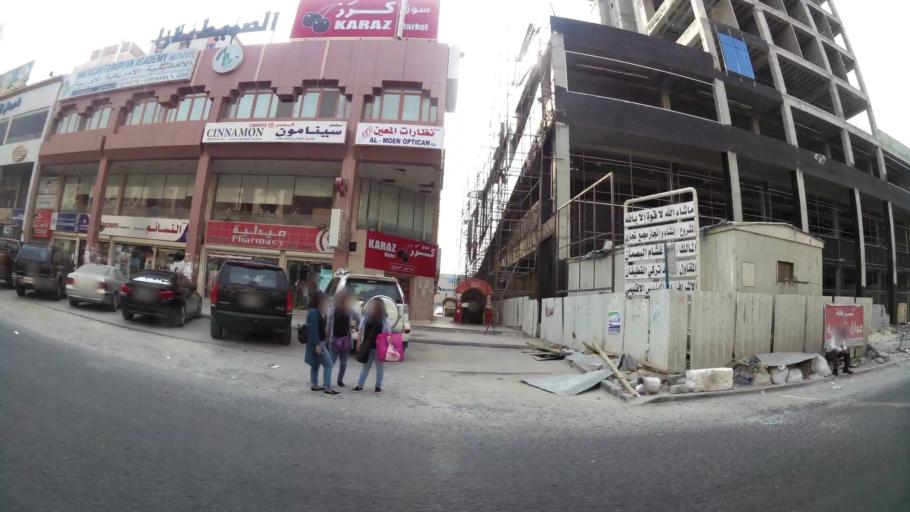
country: KW
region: Al Farwaniyah
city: Al Farwaniyah
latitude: 29.2775
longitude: 47.9624
